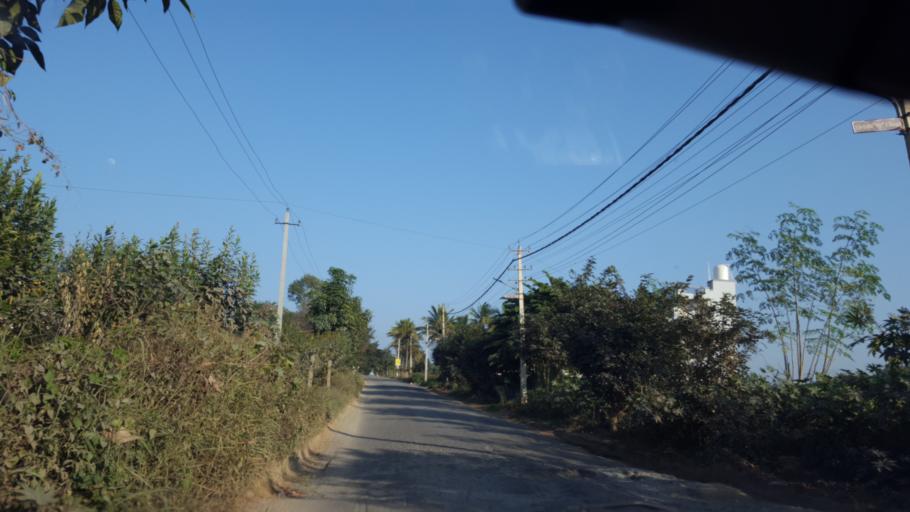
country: IN
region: Karnataka
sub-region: Bangalore Rural
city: Hoskote
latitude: 12.9148
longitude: 77.7663
